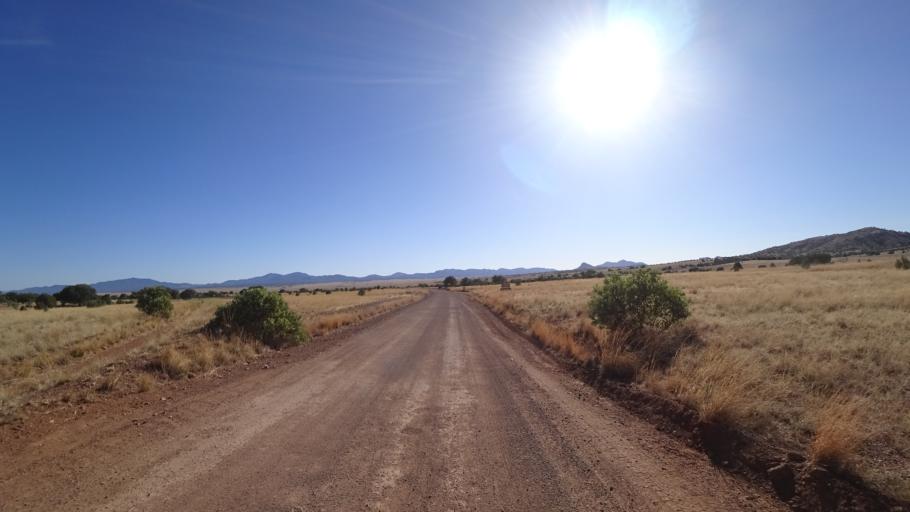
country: MX
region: Sonora
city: Santa Cruz
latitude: 31.4821
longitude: -110.5672
